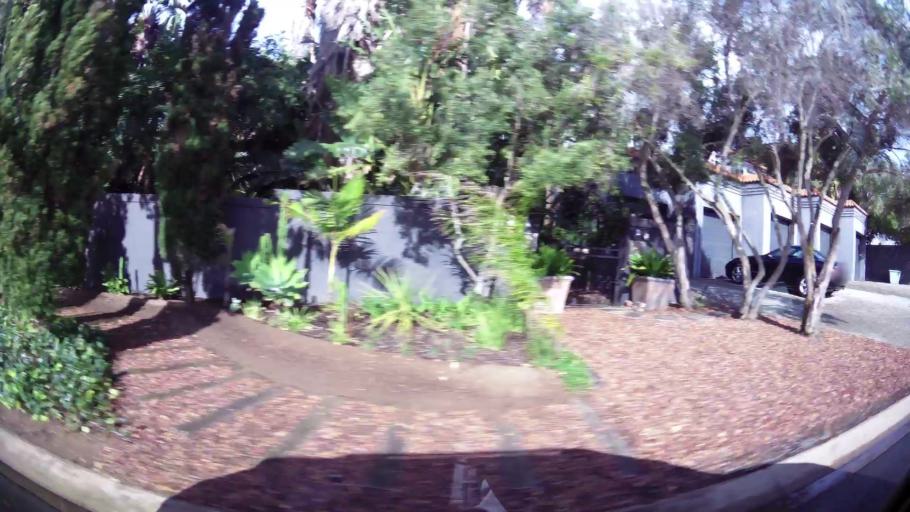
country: ZA
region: Western Cape
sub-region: Eden District Municipality
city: Mossel Bay
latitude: -34.1904
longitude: 22.1384
